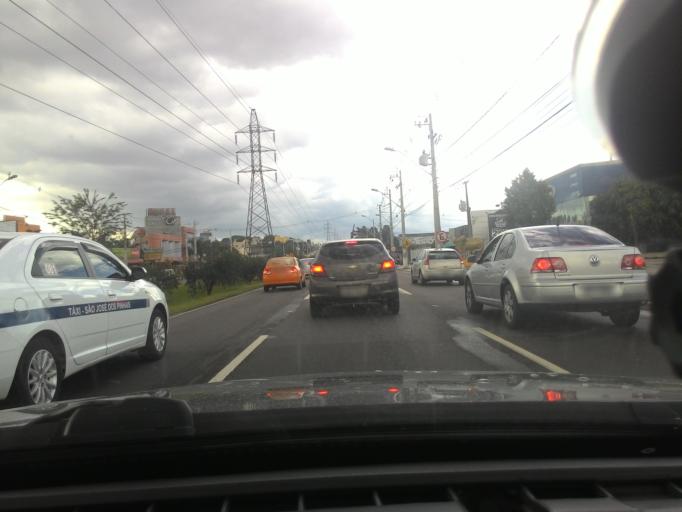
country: BR
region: Parana
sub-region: Pinhais
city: Pinhais
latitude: -25.4755
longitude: -49.2267
